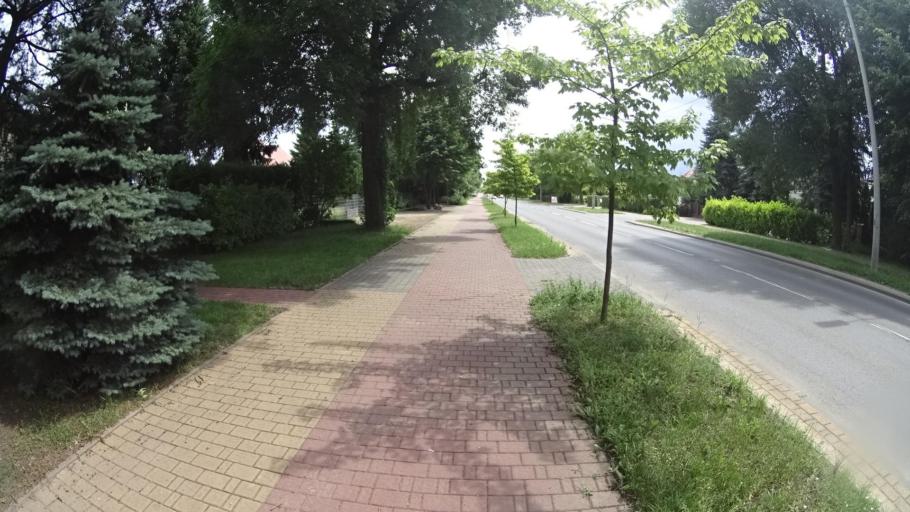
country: PL
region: Masovian Voivodeship
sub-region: Powiat grojecki
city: Grojec
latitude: 51.8556
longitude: 20.8701
